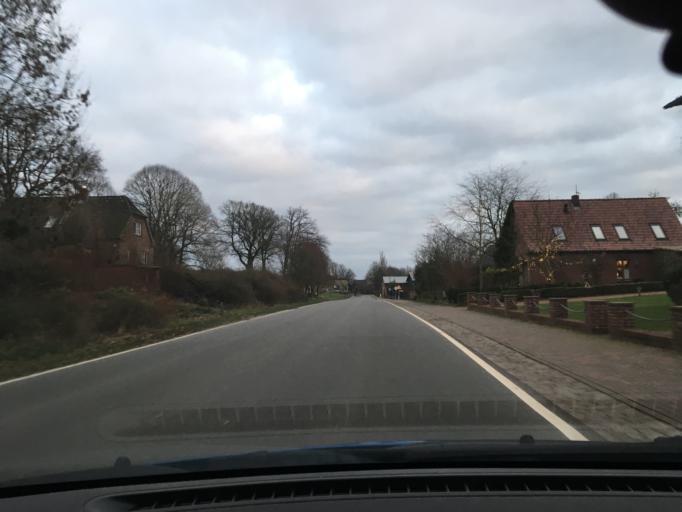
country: DE
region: Schleswig-Holstein
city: Kaaks
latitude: 53.9915
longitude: 9.4624
